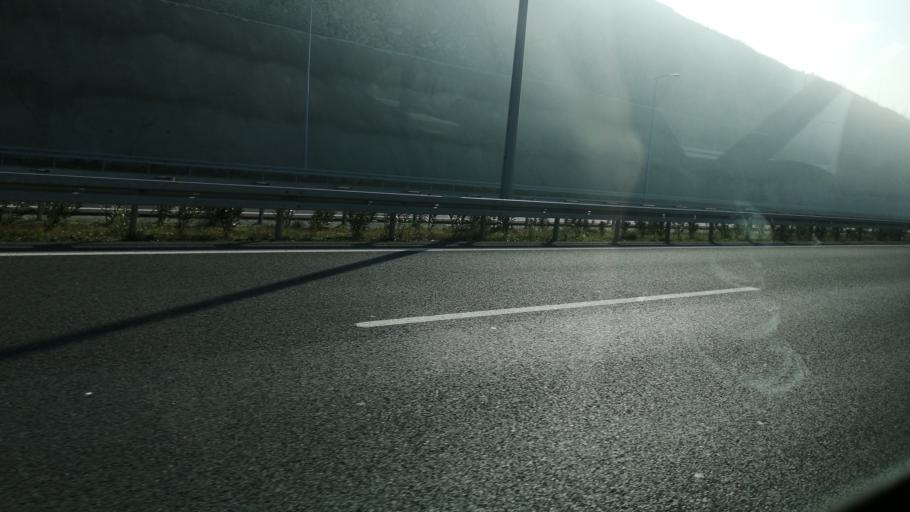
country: TR
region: Kocaeli
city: Tavsanli
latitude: 40.7791
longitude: 29.5177
